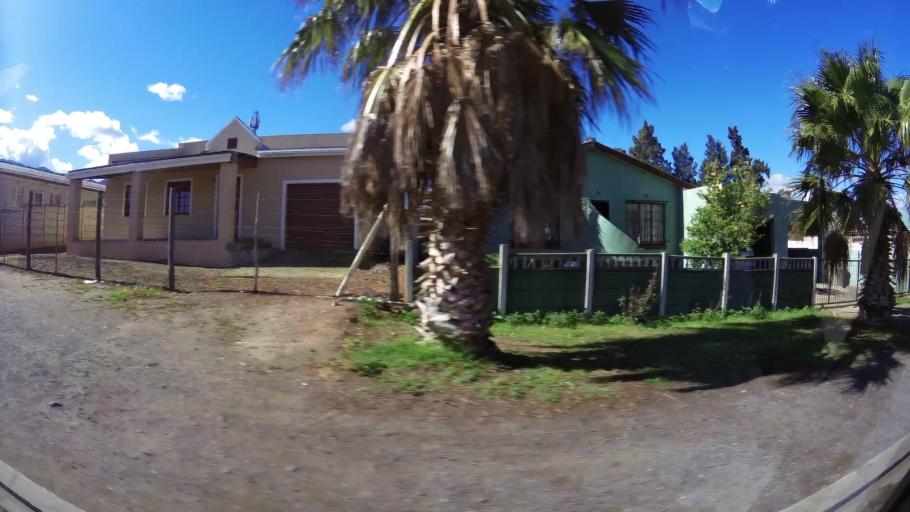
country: ZA
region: Western Cape
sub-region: Cape Winelands District Municipality
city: Ashton
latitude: -33.7932
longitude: 19.8946
